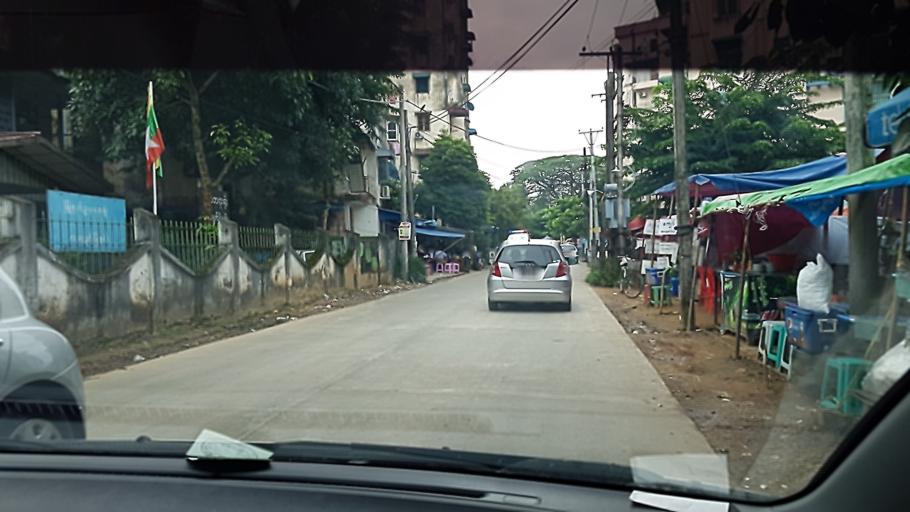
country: MM
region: Yangon
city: Yangon
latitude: 16.8204
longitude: 96.1246
